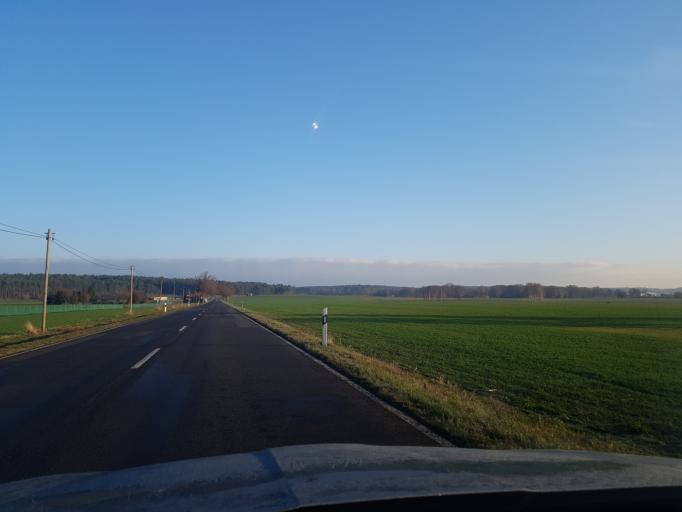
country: DE
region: Brandenburg
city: Schlieben
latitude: 51.7319
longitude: 13.4234
